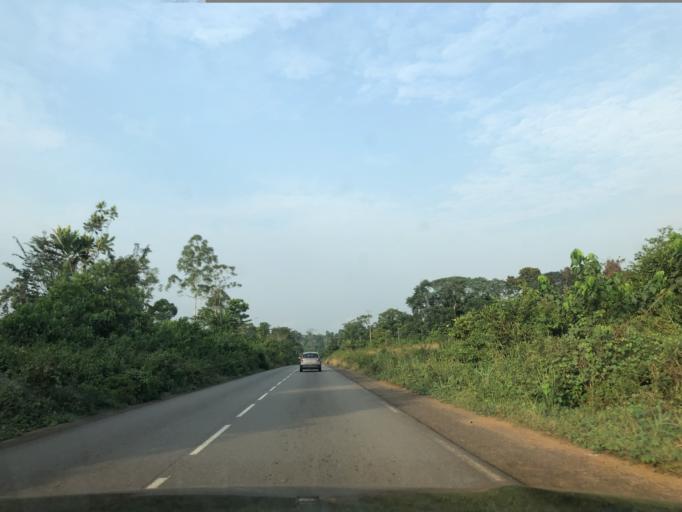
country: CM
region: Littoral
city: Dizangue
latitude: 3.3559
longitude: 10.1010
